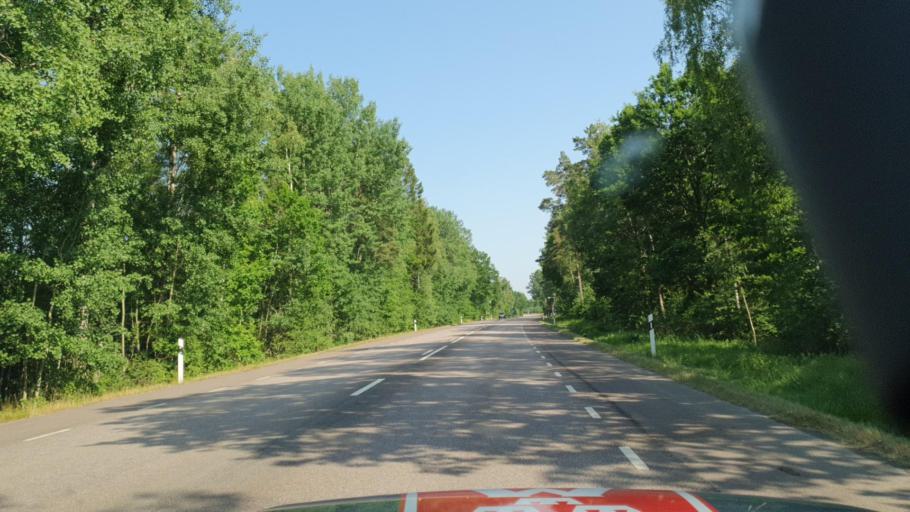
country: SE
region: Kalmar
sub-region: Nybro Kommun
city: Nybro
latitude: 56.7558
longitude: 15.8816
